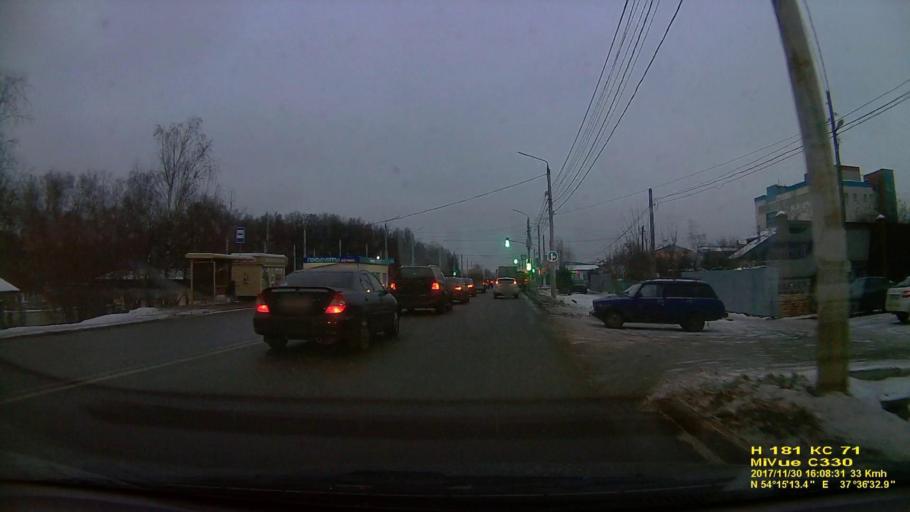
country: RU
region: Tula
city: Gorelki
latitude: 54.2536
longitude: 37.6092
